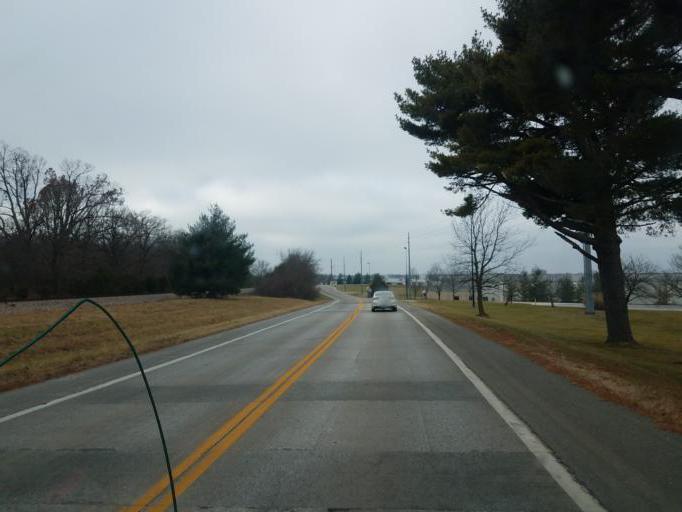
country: US
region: Missouri
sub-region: Greene County
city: Strafford
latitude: 37.2466
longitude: -93.1909
